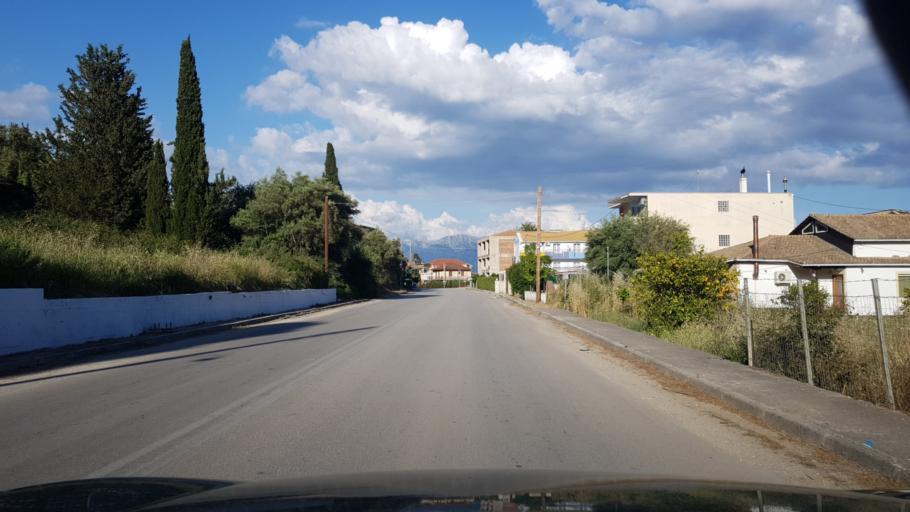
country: GR
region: Ionian Islands
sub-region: Lefkada
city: Nidri
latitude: 38.7166
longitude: 20.7151
